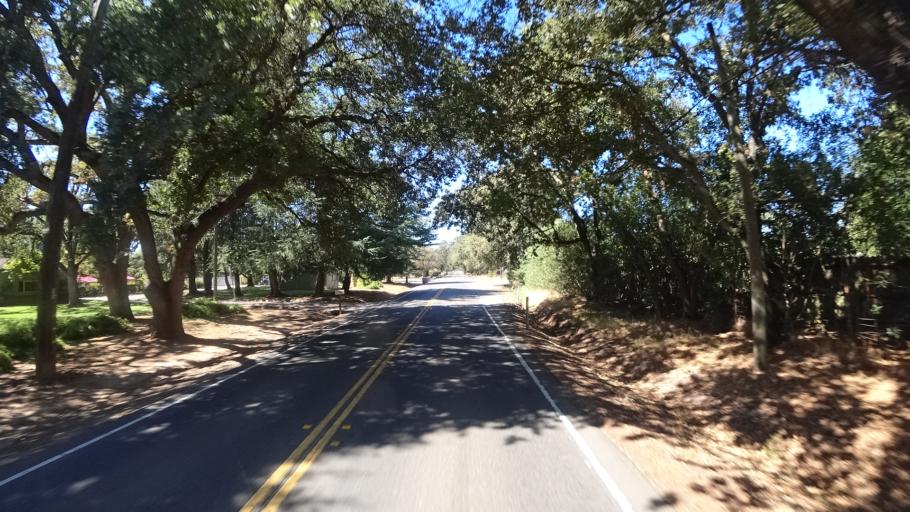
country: US
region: California
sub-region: Sacramento County
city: Wilton
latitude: 38.4382
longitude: -121.3015
